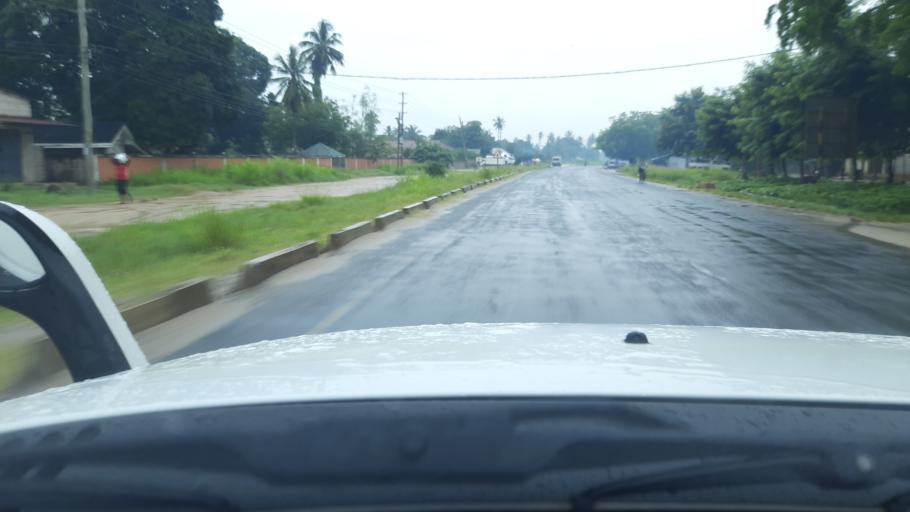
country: TZ
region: Pwani
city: Bagamoyo
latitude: -6.5096
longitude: 38.9336
